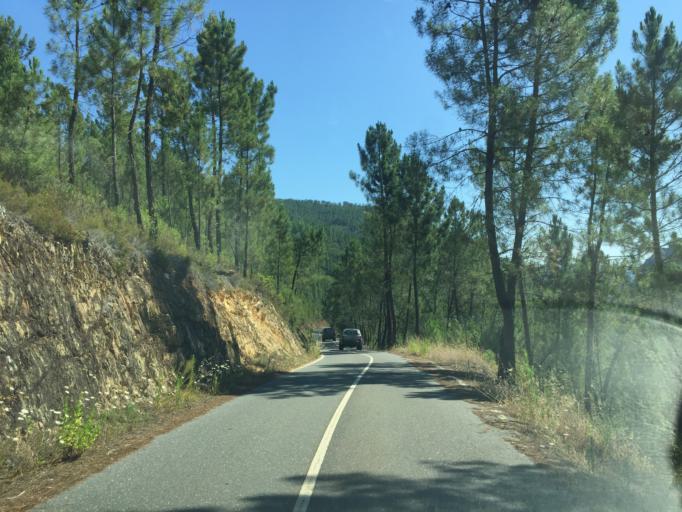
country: PT
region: Coimbra
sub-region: Pampilhosa da Serra
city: Pampilhosa da Serra
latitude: 40.0309
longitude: -7.8226
